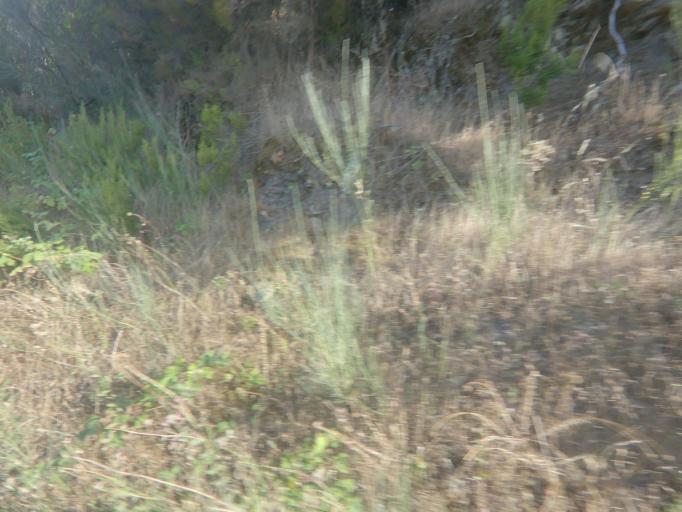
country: PT
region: Viseu
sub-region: Tabuaco
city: Tabuaco
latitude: 41.1486
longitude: -7.5953
